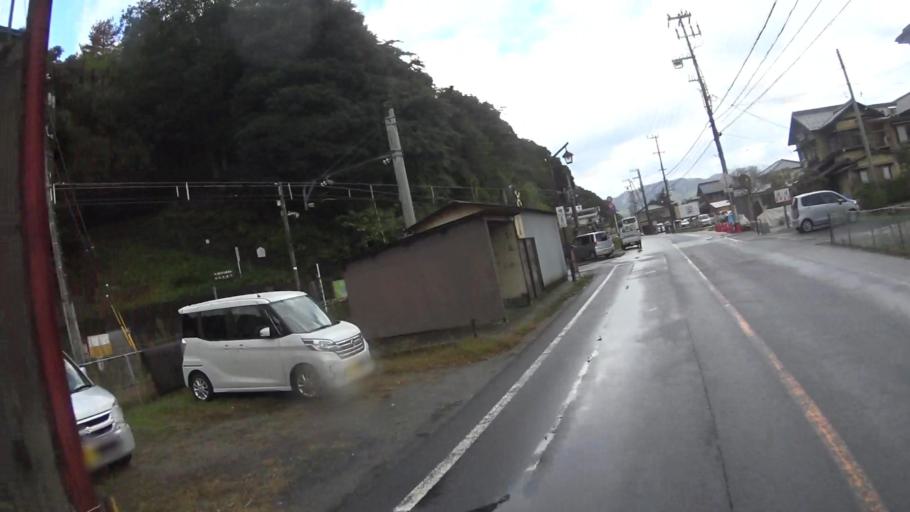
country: JP
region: Kyoto
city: Miyazu
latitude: 35.5585
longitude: 135.1802
